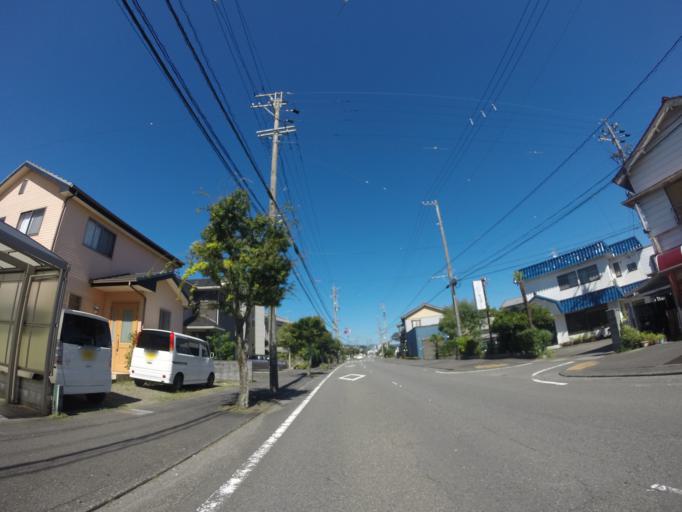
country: JP
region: Shizuoka
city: Kanaya
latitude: 34.8365
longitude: 138.1520
